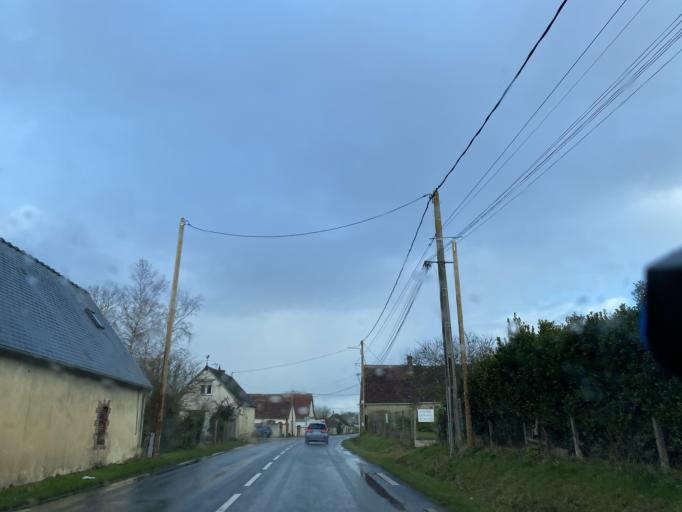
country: FR
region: Centre
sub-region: Departement d'Eure-et-Loir
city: Chateauneuf-en-Thymerais
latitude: 48.5507
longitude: 1.2941
